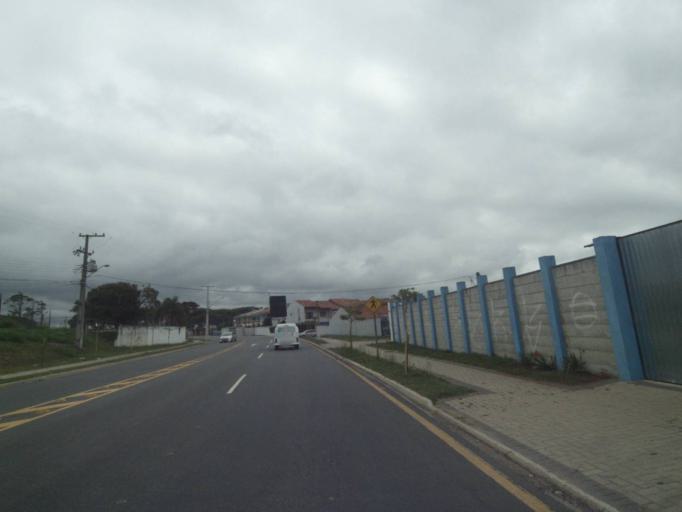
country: BR
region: Parana
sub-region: Pinhais
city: Pinhais
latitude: -25.4321
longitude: -49.2173
